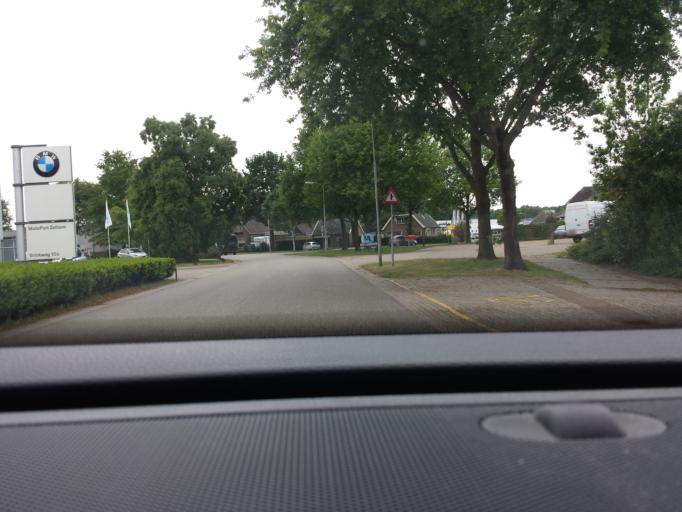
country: NL
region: Gelderland
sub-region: Gemeente Bronckhorst
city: Zelhem
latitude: 52.0025
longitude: 6.3537
